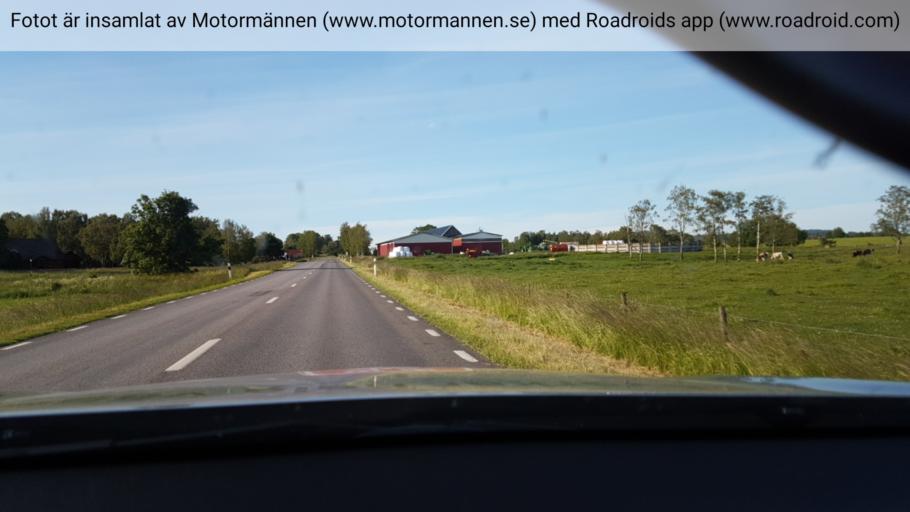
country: SE
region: Vaestra Goetaland
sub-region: Falkopings Kommun
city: Falkoeping
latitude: 58.0942
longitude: 13.5262
